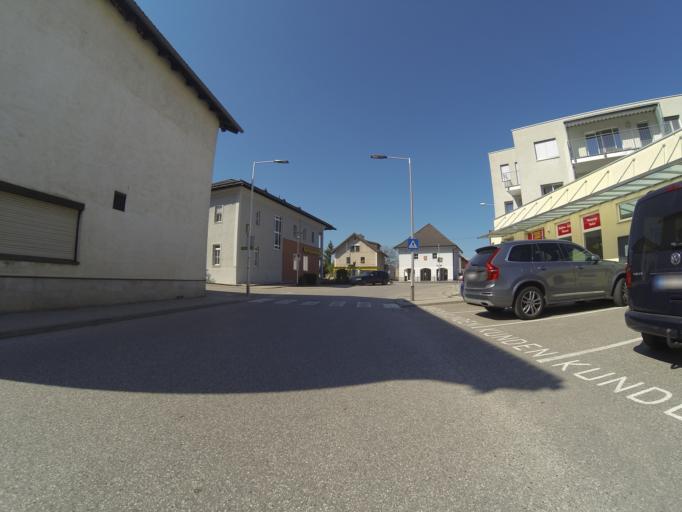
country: AT
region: Upper Austria
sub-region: Politischer Bezirk Gmunden
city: Altmunster
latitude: 47.9296
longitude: 13.7708
